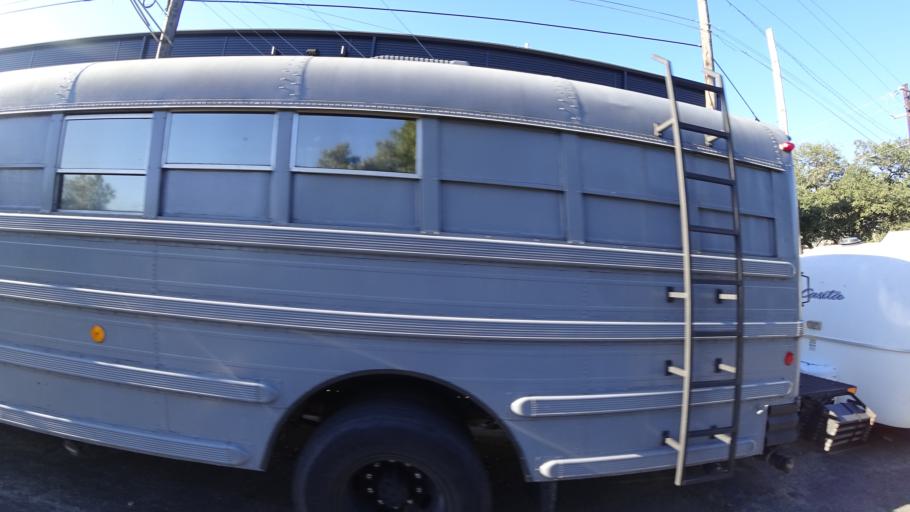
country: US
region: Texas
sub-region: Travis County
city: Austin
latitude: 30.2277
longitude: -97.7630
